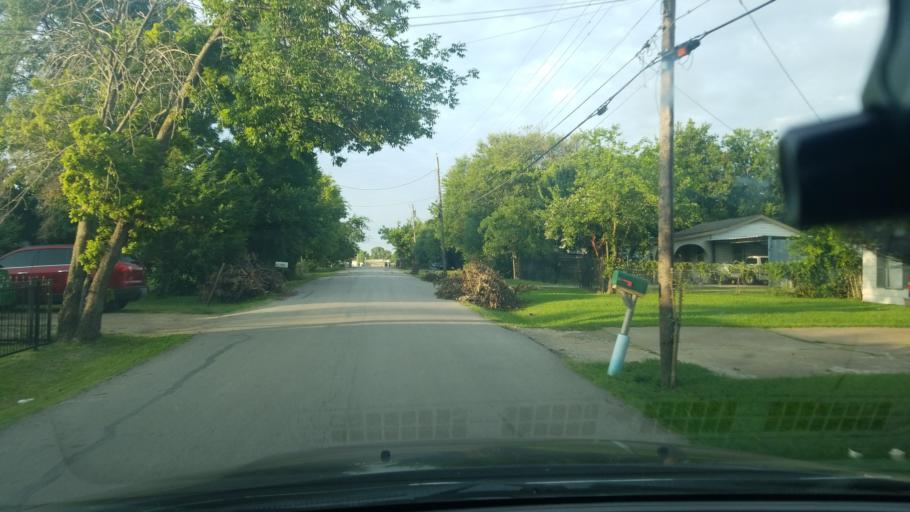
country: US
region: Texas
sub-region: Dallas County
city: Balch Springs
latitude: 32.7481
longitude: -96.6334
